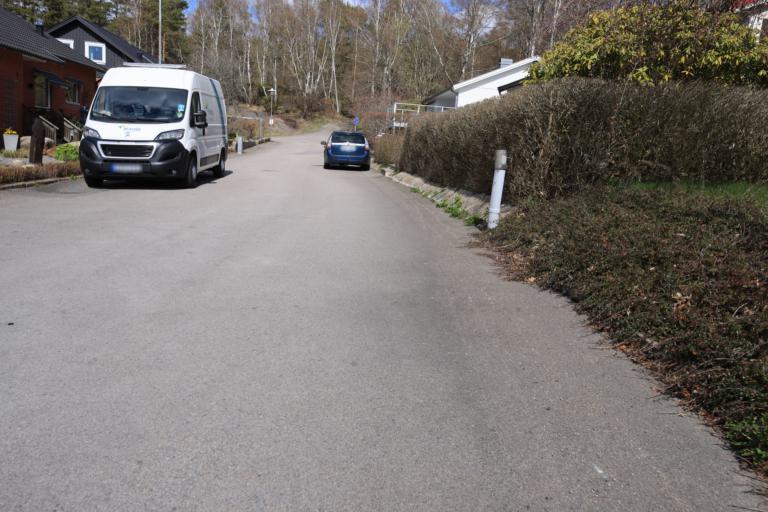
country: SE
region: Halland
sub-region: Varbergs Kommun
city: Varberg
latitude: 57.1754
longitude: 12.2309
